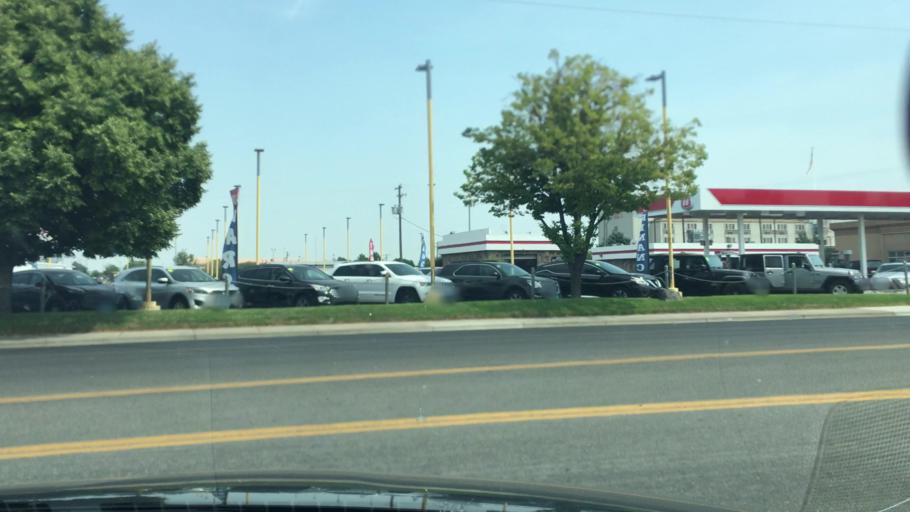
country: US
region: Idaho
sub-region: Twin Falls County
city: Twin Falls
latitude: 42.5908
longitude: -114.4602
